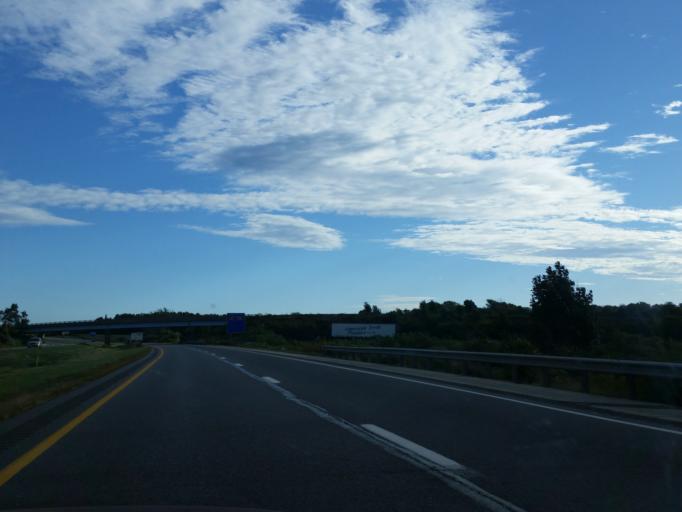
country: US
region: Pennsylvania
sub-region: Erie County
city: North East
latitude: 42.2225
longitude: -79.7868
